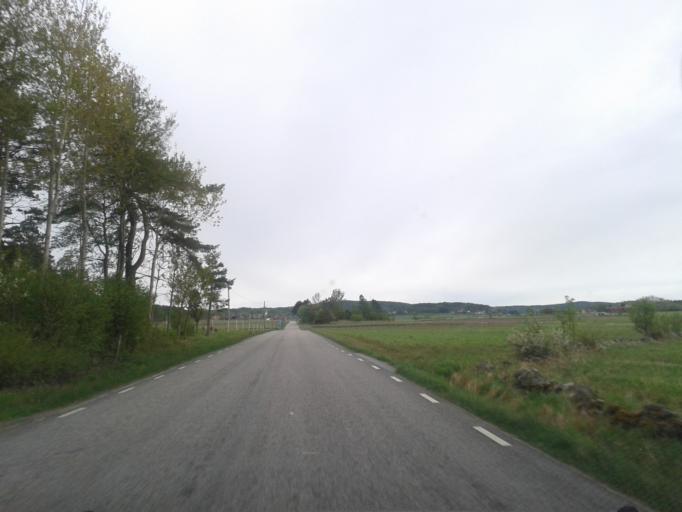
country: SE
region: Vaestra Goetaland
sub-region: Kungalvs Kommun
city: Kode
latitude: 57.9594
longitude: 11.8223
